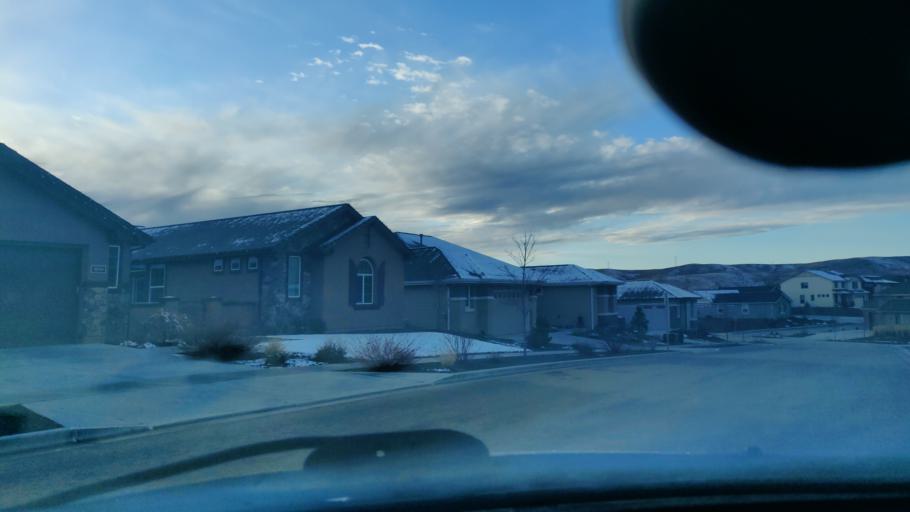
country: US
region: Idaho
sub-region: Ada County
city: Eagle
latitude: 43.7734
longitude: -116.2514
